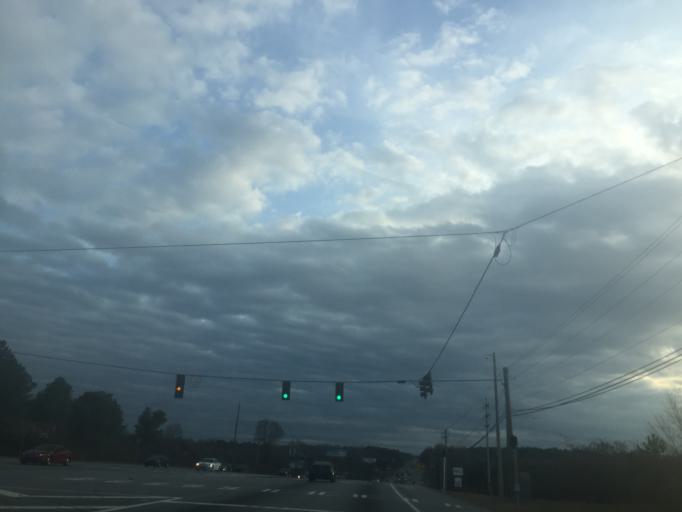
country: US
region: Georgia
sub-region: Clayton County
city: Forest Park
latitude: 33.6096
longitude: -84.4033
